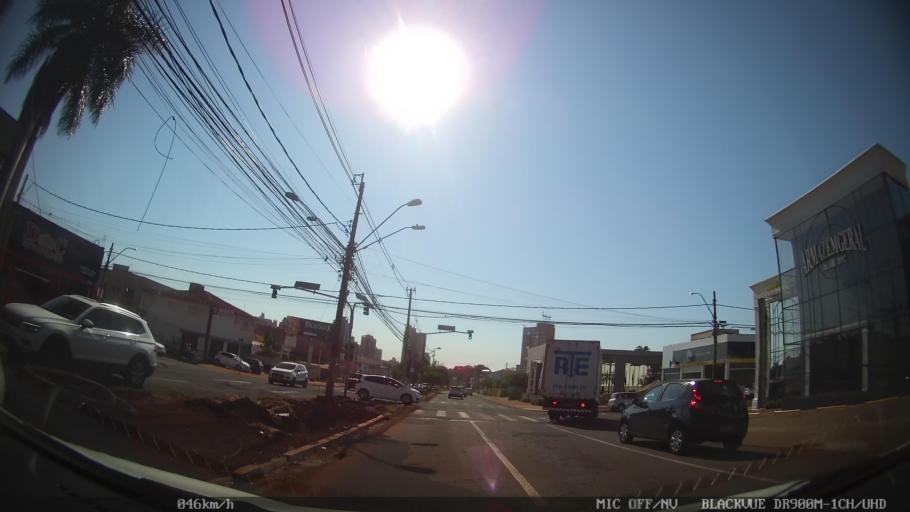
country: BR
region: Sao Paulo
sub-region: Ribeirao Preto
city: Ribeirao Preto
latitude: -21.1906
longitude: -47.8091
